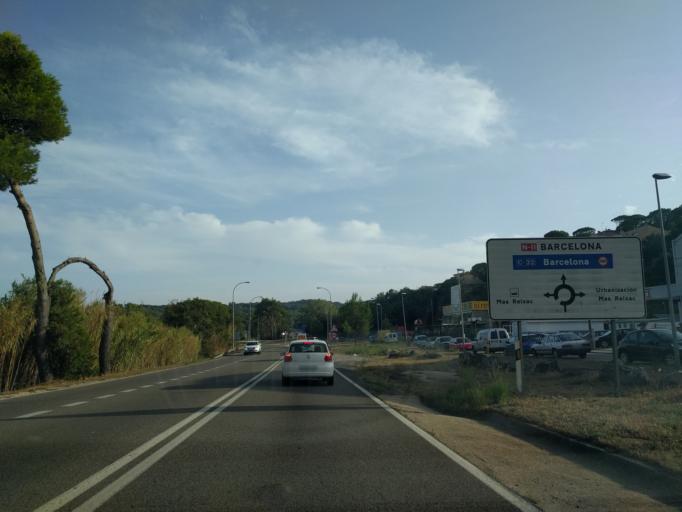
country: ES
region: Catalonia
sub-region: Provincia de Barcelona
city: Tordera
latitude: 41.6854
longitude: 2.7218
